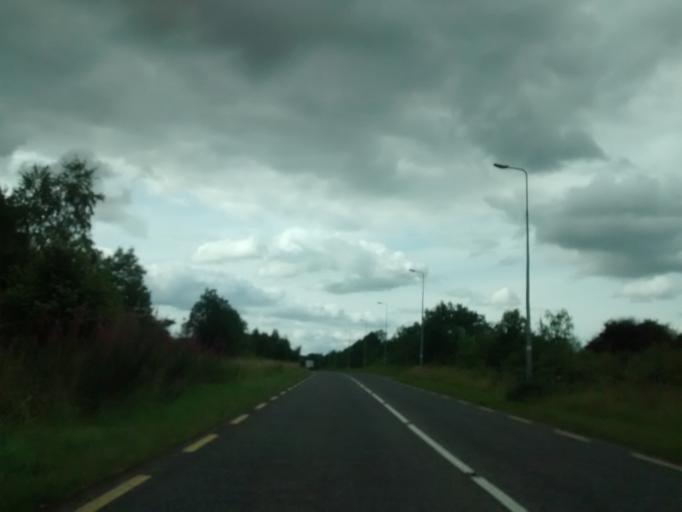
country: IE
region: Leinster
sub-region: An Iarmhi
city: Moate
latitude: 53.3903
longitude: -7.6850
